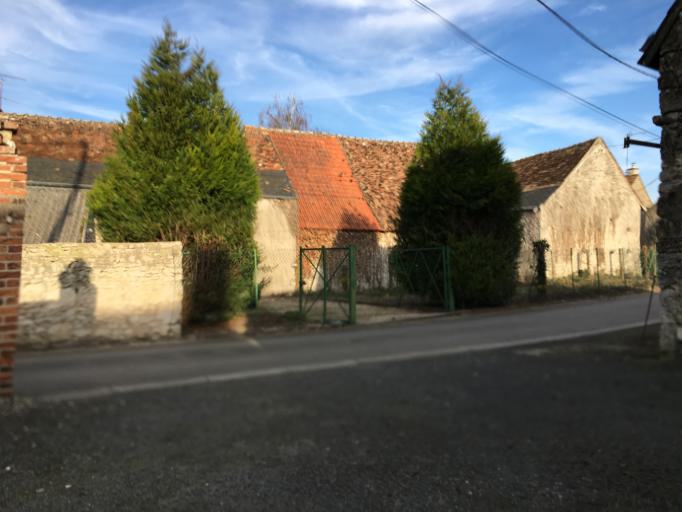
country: FR
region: Centre
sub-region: Departement du Loir-et-Cher
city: Mer
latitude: 47.7570
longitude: 1.5019
